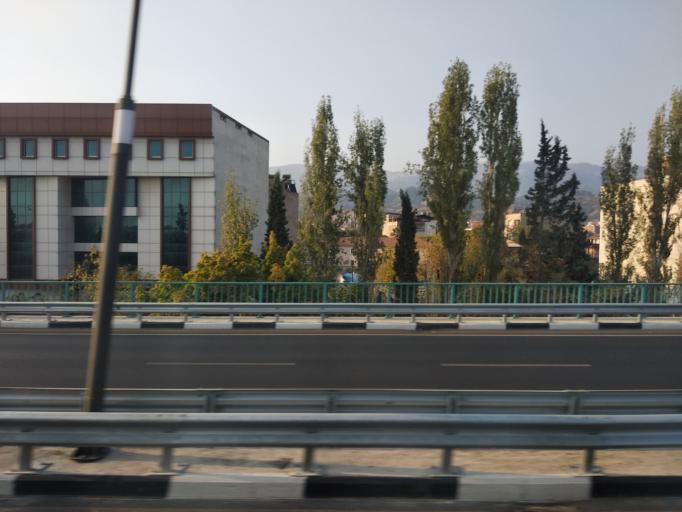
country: TR
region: Manisa
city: Salihli
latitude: 38.4903
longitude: 28.1397
